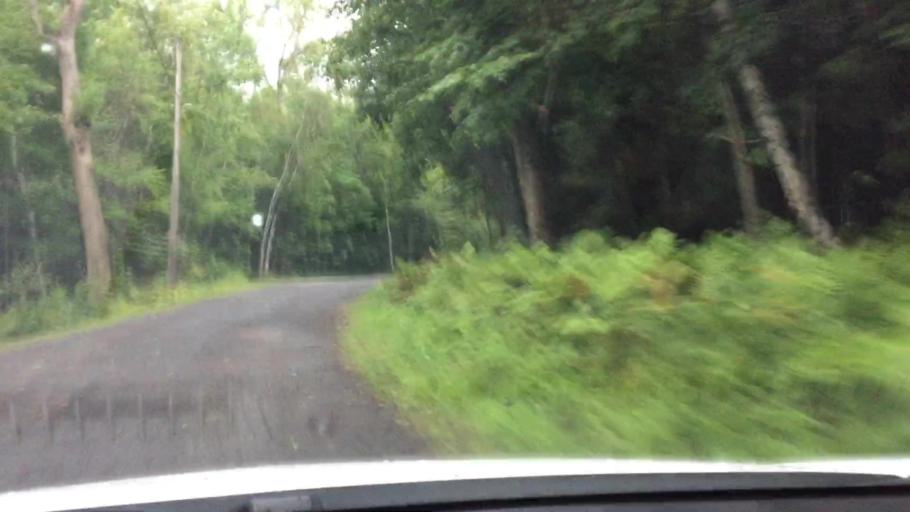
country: US
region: Massachusetts
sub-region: Berkshire County
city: Otis
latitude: 42.1487
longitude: -73.0500
